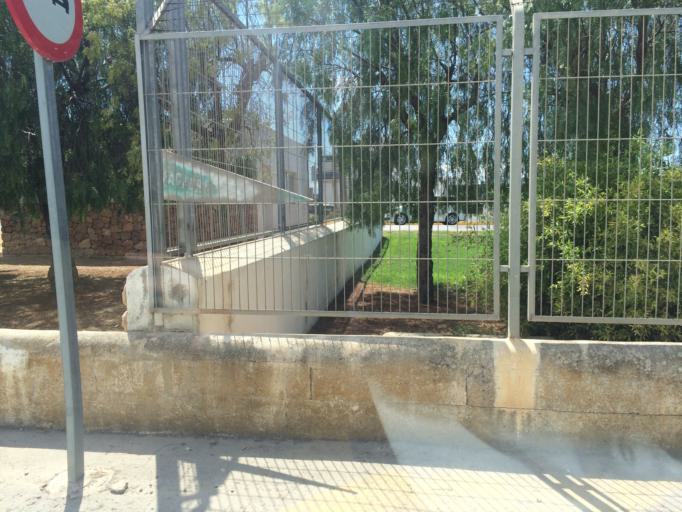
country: ES
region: Balearic Islands
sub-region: Illes Balears
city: Ibiza
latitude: 38.8788
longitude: 1.3690
